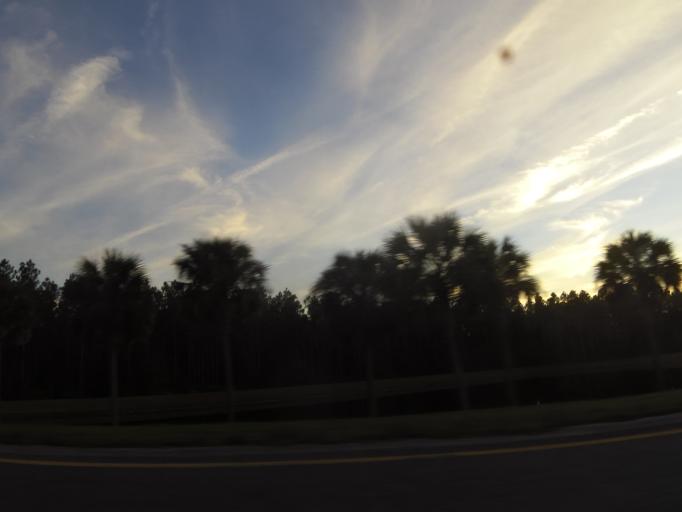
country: US
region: Florida
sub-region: Saint Johns County
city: Palm Valley
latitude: 30.1027
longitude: -81.4707
